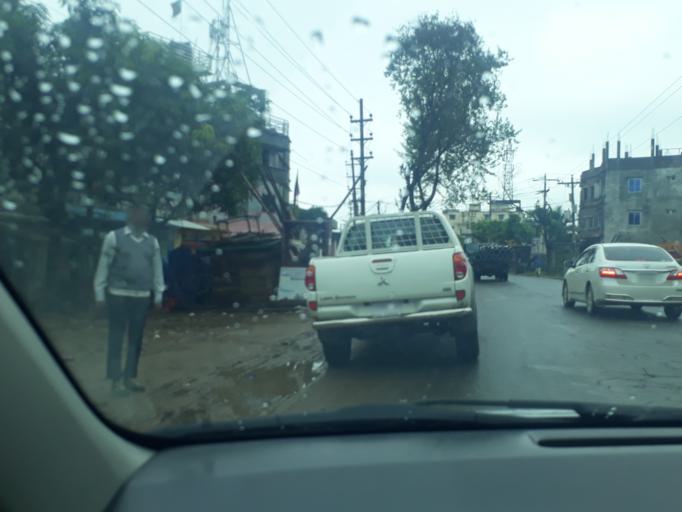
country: BD
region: Dhaka
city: Tungi
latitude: 23.9044
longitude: 90.3244
